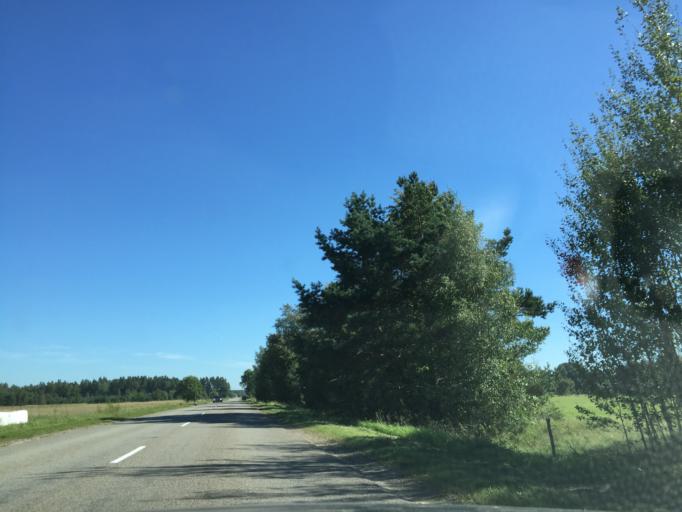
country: LV
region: Akniste
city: Akniste
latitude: 56.1491
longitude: 25.7835
